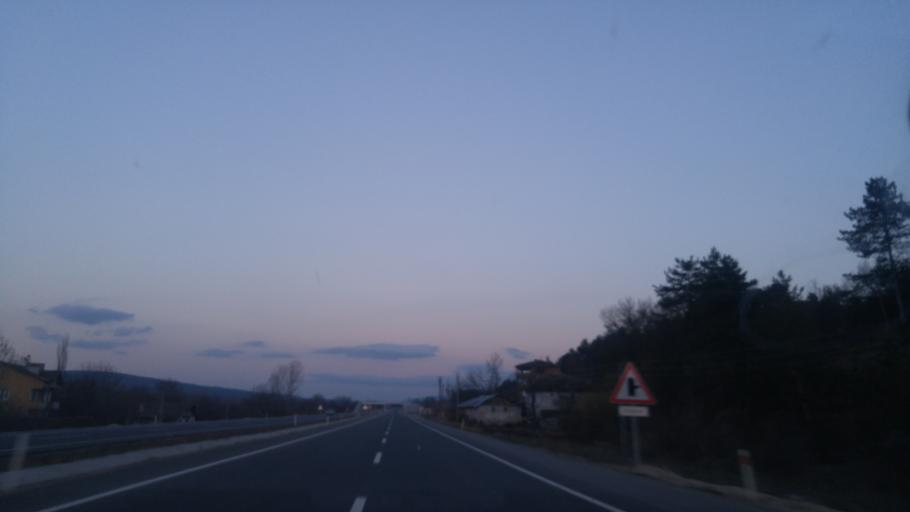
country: TR
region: Kastamonu
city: Igdir
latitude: 41.2289
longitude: 33.0902
